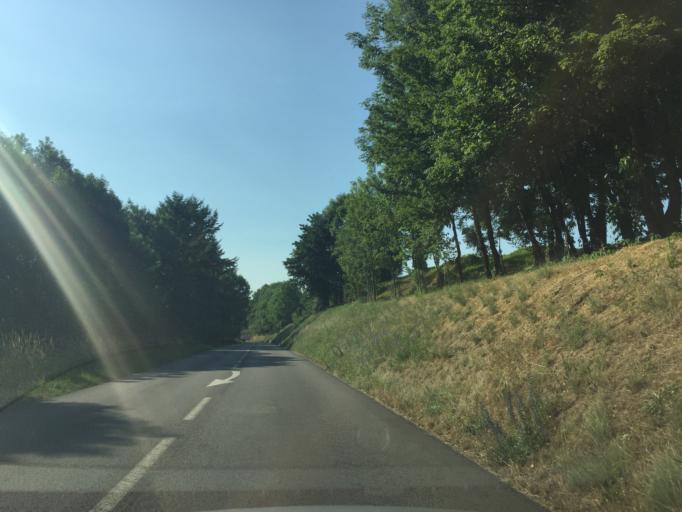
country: FR
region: Rhone-Alpes
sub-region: Departement de la Drome
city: Saint-Laurent-en-Royans
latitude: 45.0289
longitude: 5.3203
